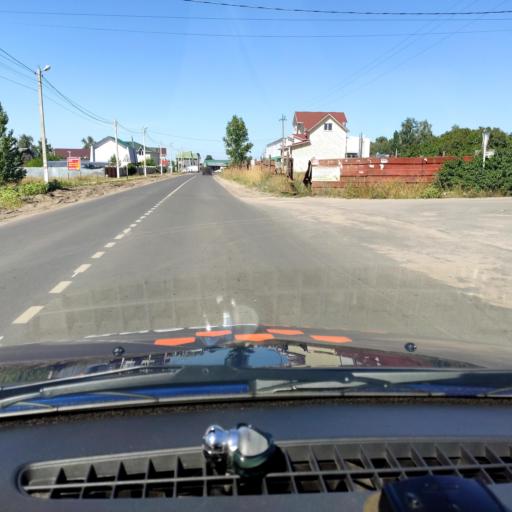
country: RU
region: Voronezj
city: Podgornoye
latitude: 51.7883
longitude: 39.1460
